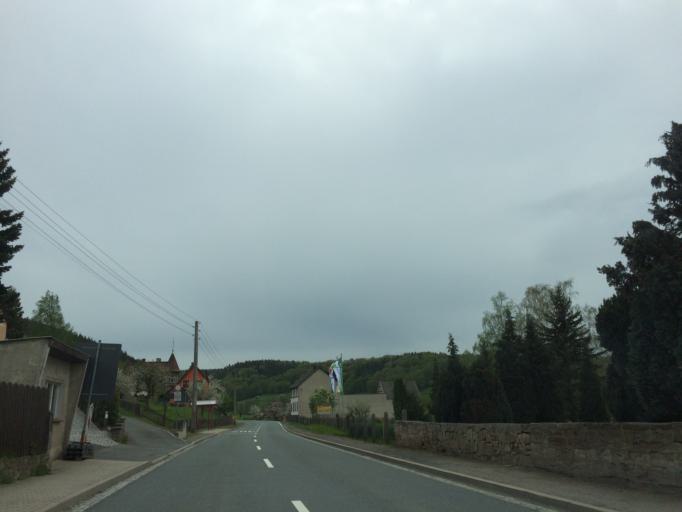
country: DE
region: Thuringia
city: Freienorla
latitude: 50.7688
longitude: 11.5427
